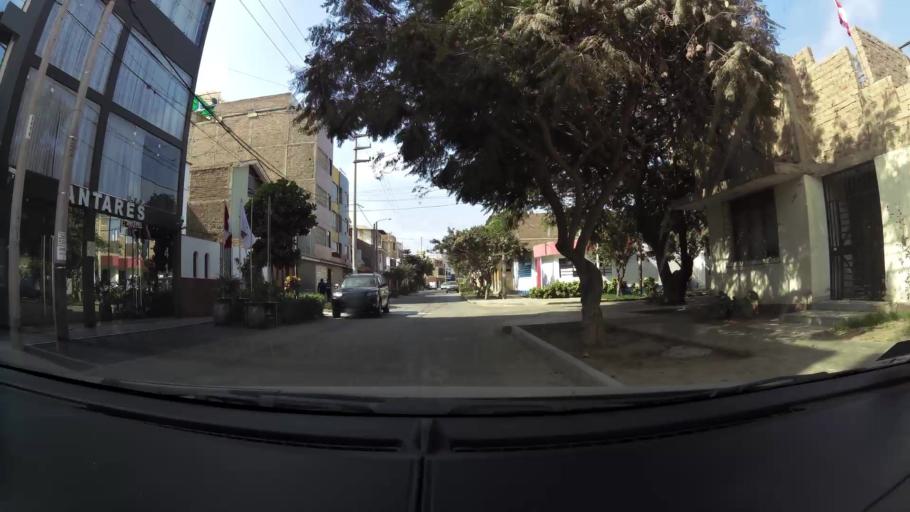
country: PE
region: La Libertad
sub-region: Provincia de Trujillo
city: Trujillo
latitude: -8.1258
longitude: -79.0191
